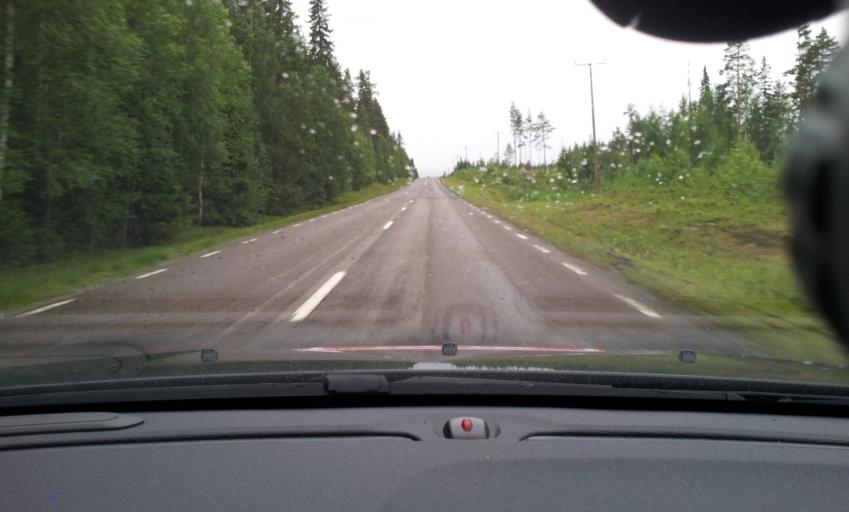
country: SE
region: Jaemtland
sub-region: Ragunda Kommun
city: Hammarstrand
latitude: 63.2012
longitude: 15.9442
